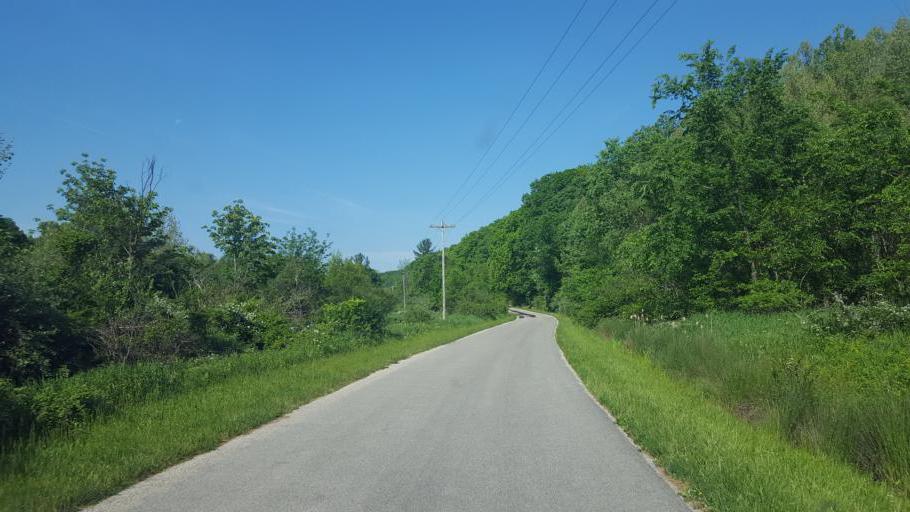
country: US
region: Ohio
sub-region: Jackson County
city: Wellston
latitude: 39.0017
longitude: -82.4806
